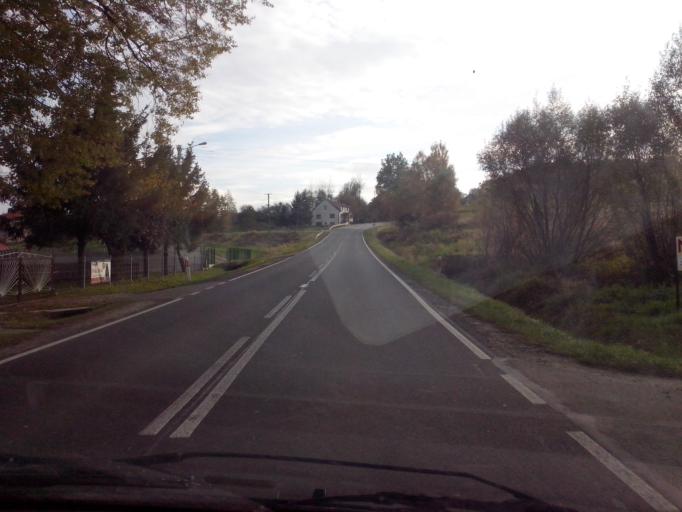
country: PL
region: Subcarpathian Voivodeship
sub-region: Powiat ropczycko-sedziszowski
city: Wielopole Skrzynskie
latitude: 49.9404
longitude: 21.6163
